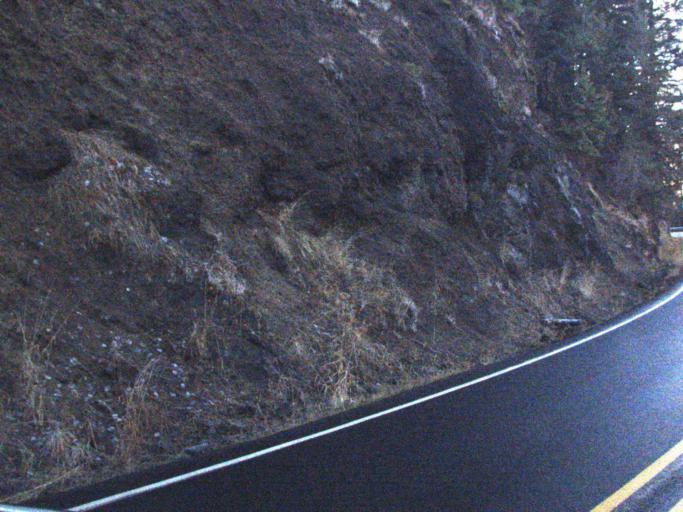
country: US
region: Washington
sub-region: Asotin County
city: Asotin
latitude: 46.0806
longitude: -117.1910
